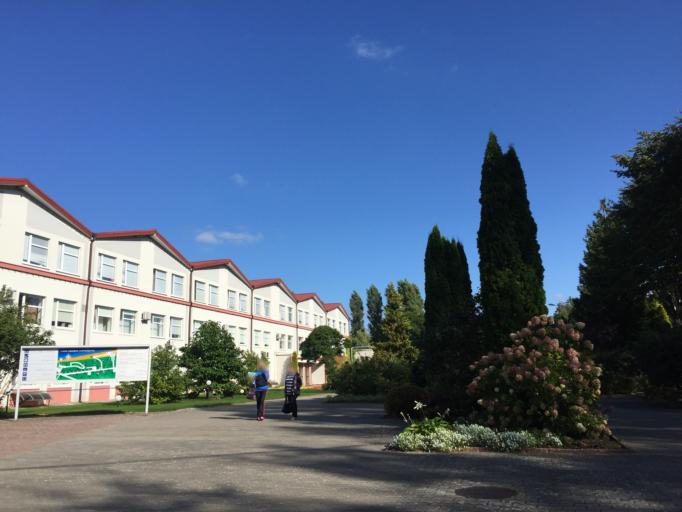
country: RU
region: Kaliningrad
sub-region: Gorod Svetlogorsk
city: Svetlogorsk
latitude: 54.9429
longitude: 20.1352
